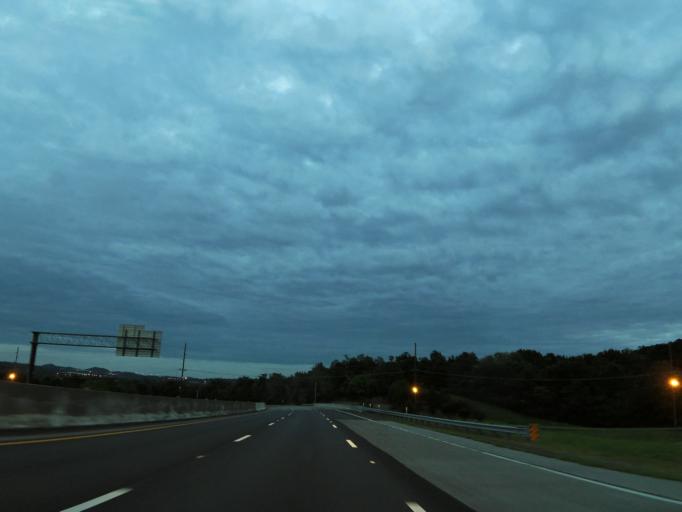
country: US
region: Tennessee
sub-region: Davidson County
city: Nashville
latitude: 36.2291
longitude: -86.8359
